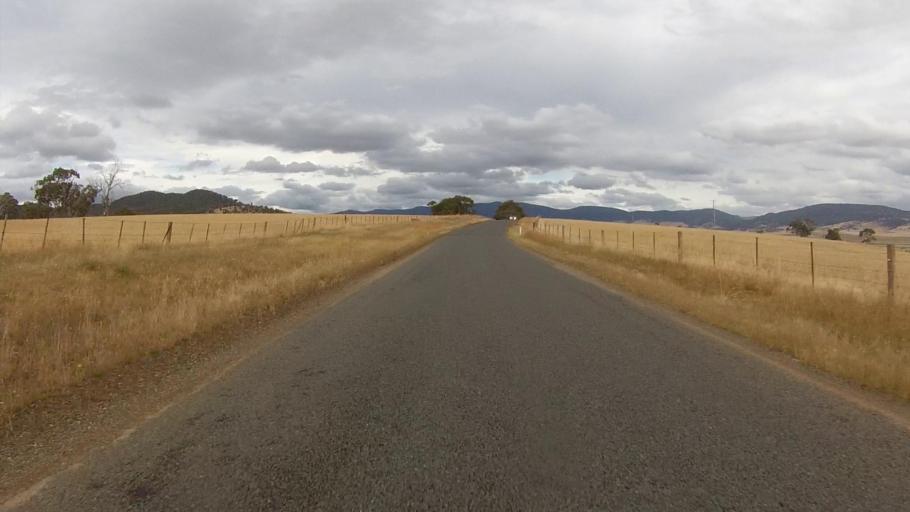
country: AU
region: Tasmania
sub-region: Northern Midlands
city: Evandale
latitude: -41.7929
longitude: 147.7439
